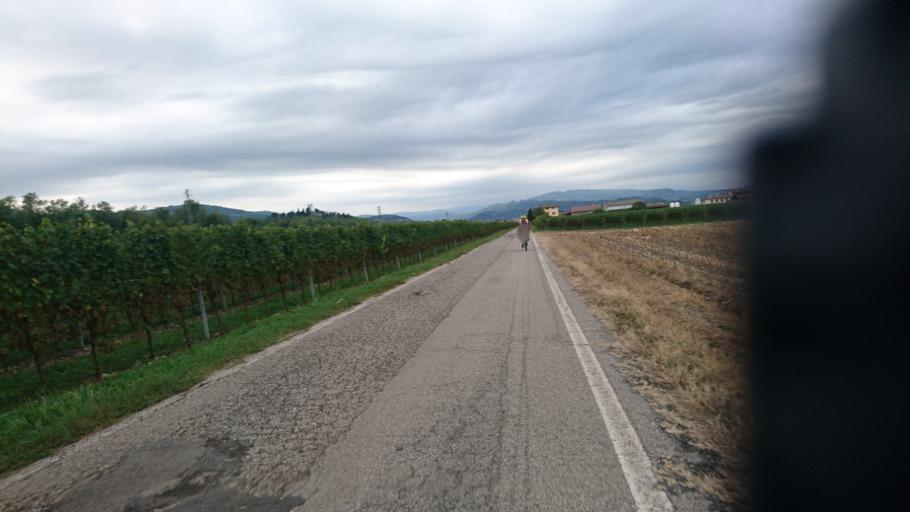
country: IT
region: Veneto
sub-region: Provincia di Vicenza
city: Zermeghedo
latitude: 45.4852
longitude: 11.3783
